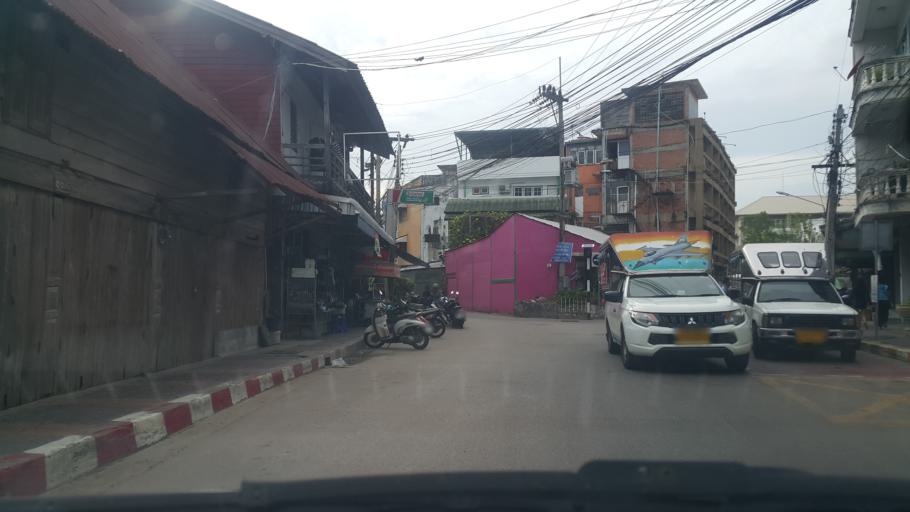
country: TH
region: Chon Buri
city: Phatthaya
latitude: 12.9725
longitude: 100.9070
